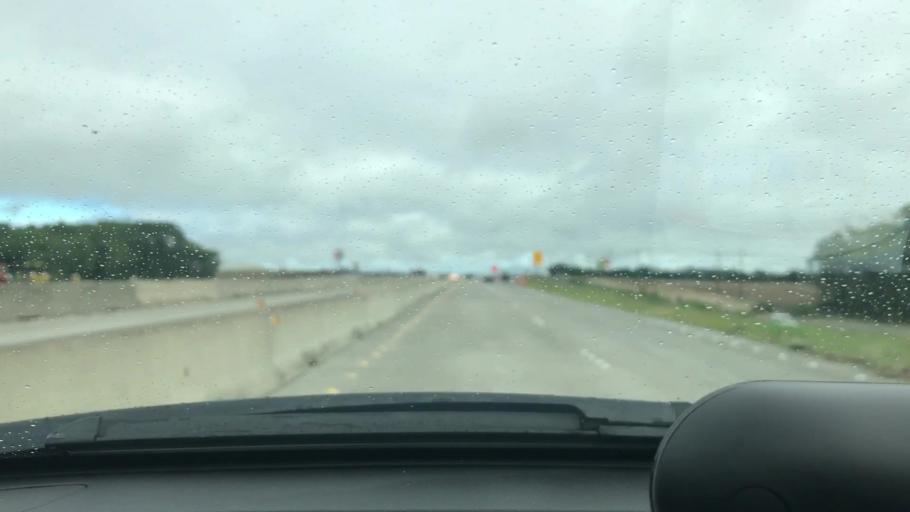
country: US
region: Texas
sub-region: Collin County
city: Anna
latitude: 33.3366
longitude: -96.5879
